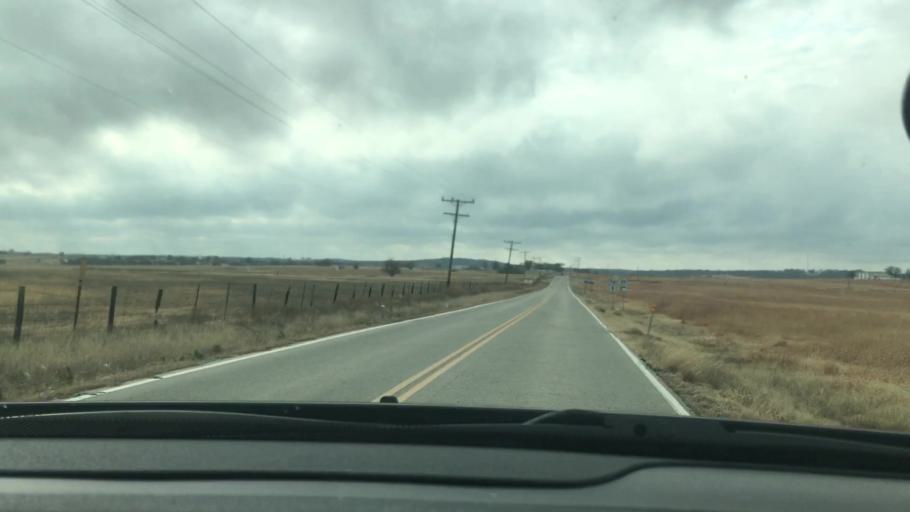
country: US
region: Oklahoma
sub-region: Bryan County
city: Durant
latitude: 34.1036
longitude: -96.4877
